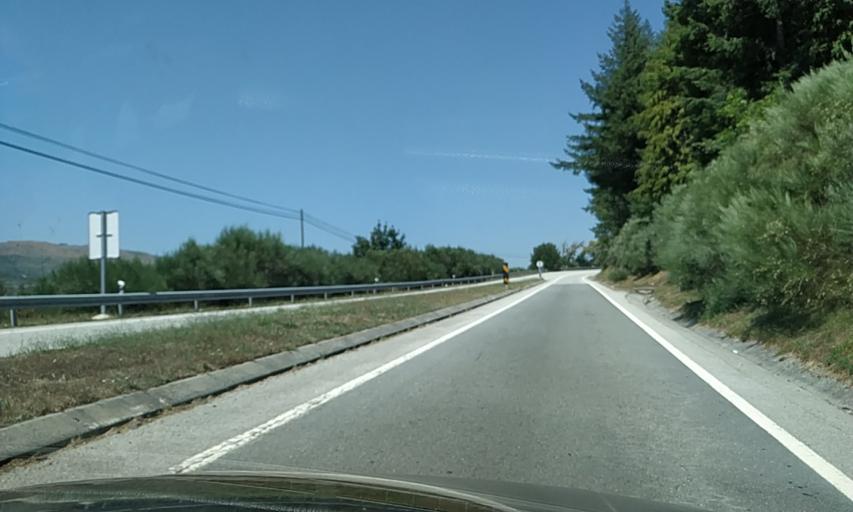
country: PT
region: Viseu
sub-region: Castro Daire
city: Castro Daire
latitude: 40.9401
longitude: -7.9122
